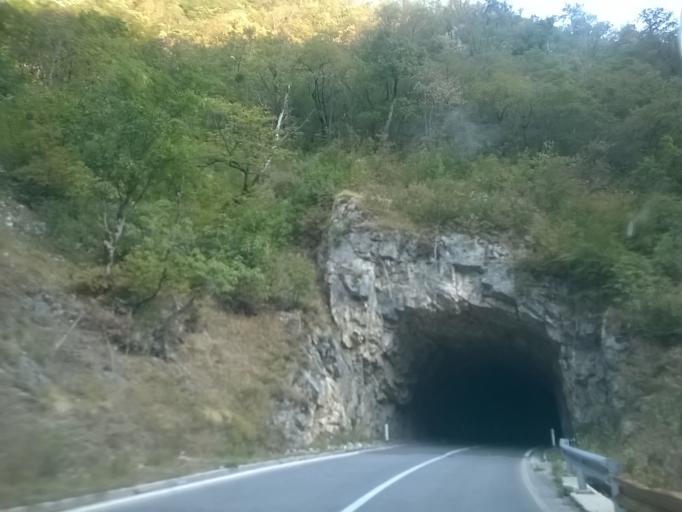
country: ME
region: Opstina Pluzine
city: Pluzine
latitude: 43.1879
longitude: 18.8518
